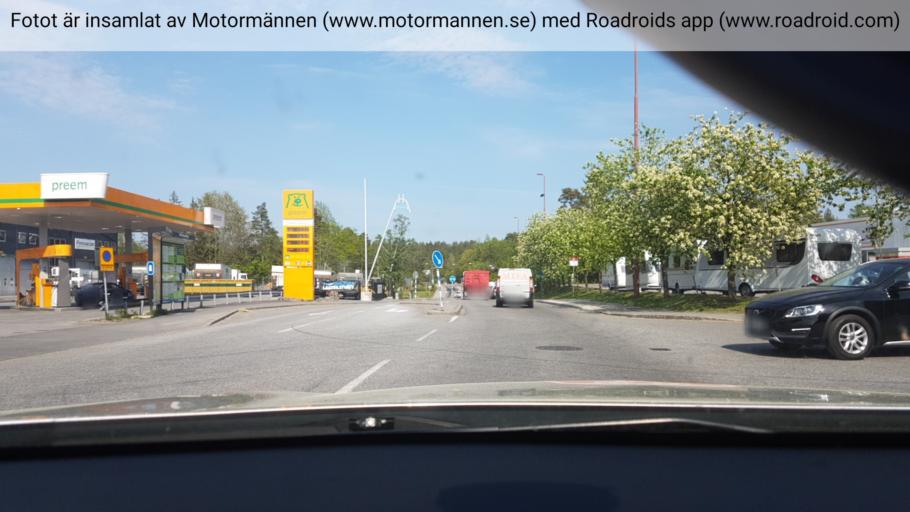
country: SE
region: Stockholm
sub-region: Stockholms Kommun
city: Arsta
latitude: 59.2623
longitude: 18.0612
